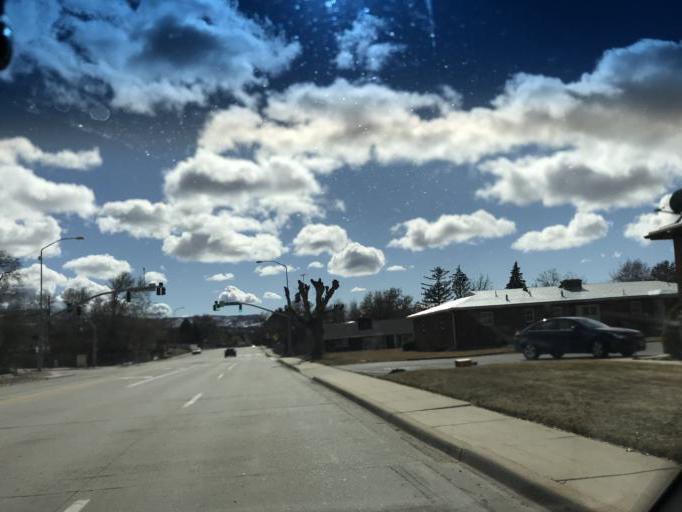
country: US
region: Utah
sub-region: Davis County
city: Bountiful
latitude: 40.8814
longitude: -111.8728
